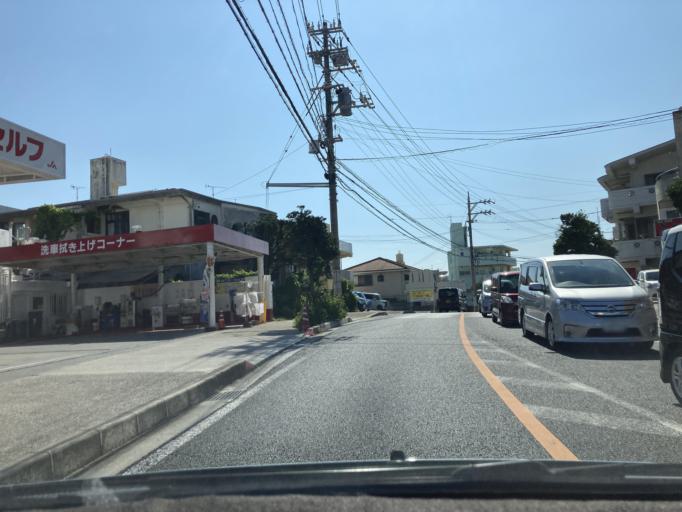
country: JP
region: Okinawa
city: Ginowan
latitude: 26.2457
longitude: 127.7260
